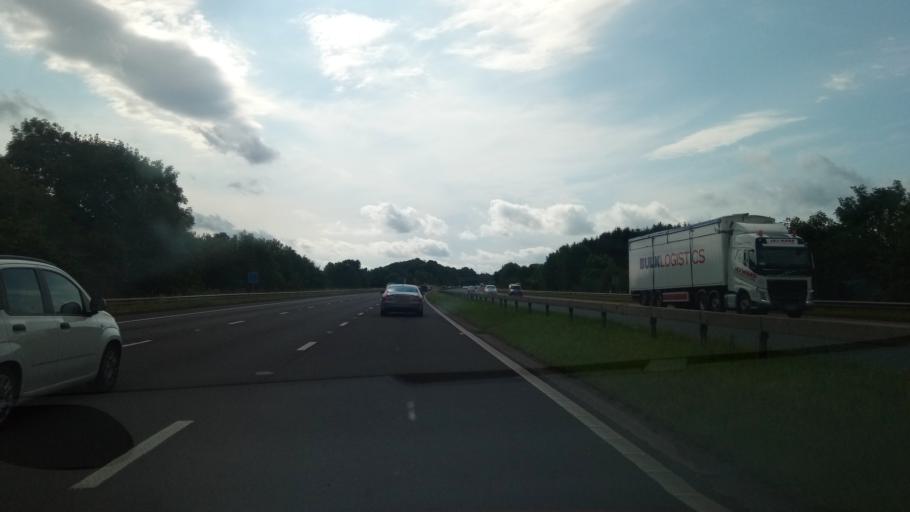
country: GB
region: England
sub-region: Cumbria
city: Penrith
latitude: 54.6417
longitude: -2.7353
